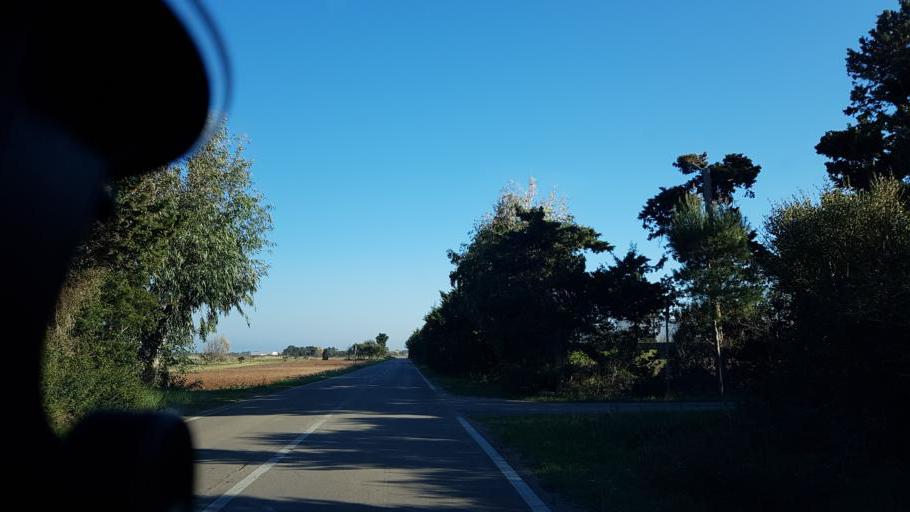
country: IT
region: Apulia
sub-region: Provincia di Lecce
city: Giorgilorio
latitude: 40.4428
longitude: 18.2322
